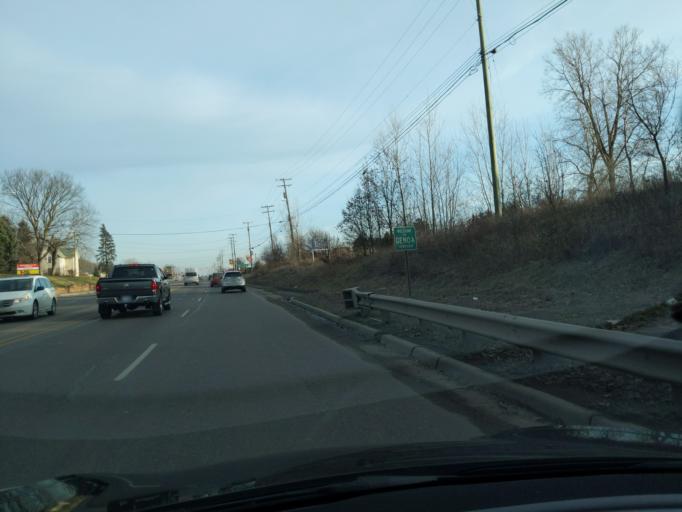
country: US
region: Michigan
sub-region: Livingston County
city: Howell
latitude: 42.6005
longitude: -83.9119
